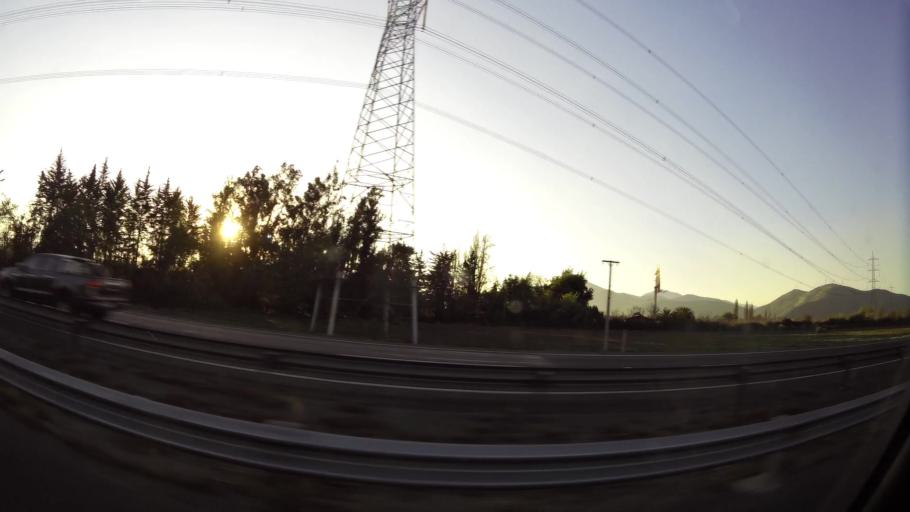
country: CL
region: Santiago Metropolitan
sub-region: Provincia de Talagante
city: Penaflor
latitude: -33.5687
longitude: -70.8476
